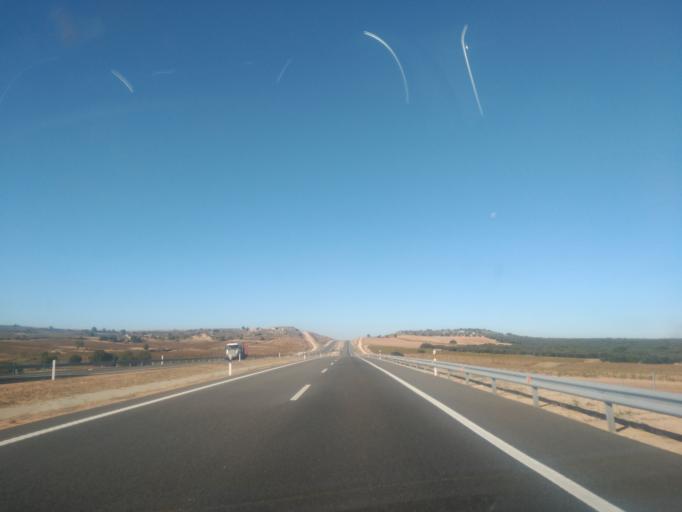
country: ES
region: Castille and Leon
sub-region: Provincia de Burgos
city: Campillo de Aranda
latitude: 41.6341
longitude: -3.7328
